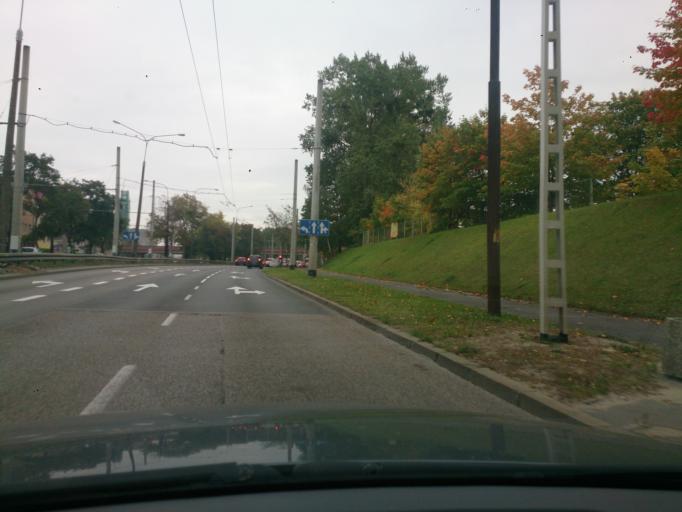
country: PL
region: Pomeranian Voivodeship
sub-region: Gdynia
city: Pogorze
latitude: 54.5338
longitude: 18.4855
